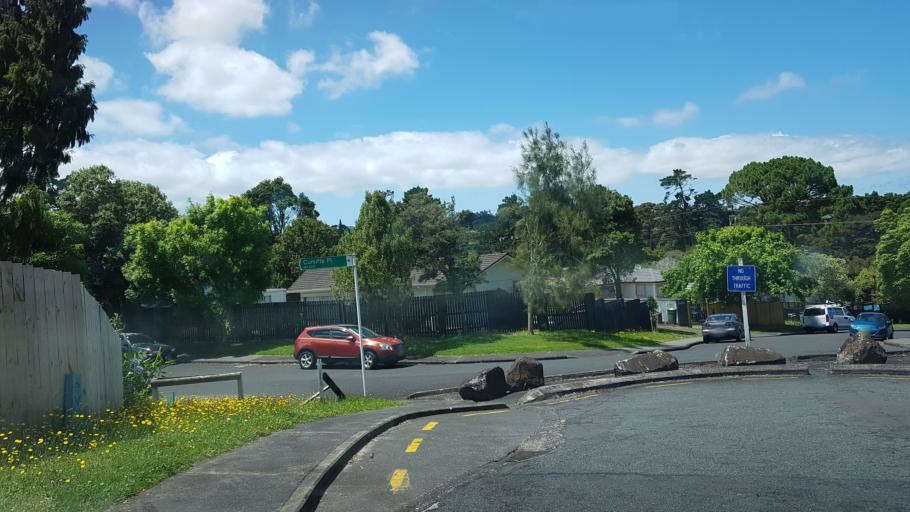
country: NZ
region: Auckland
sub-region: Auckland
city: North Shore
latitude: -36.7776
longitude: 174.7163
